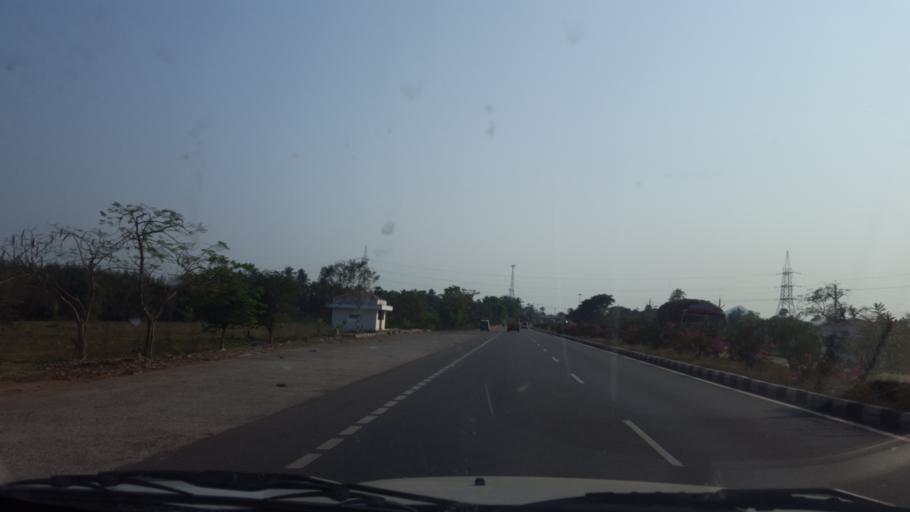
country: IN
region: Andhra Pradesh
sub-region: Vishakhapatnam
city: Elamanchili
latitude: 17.5686
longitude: 82.8624
